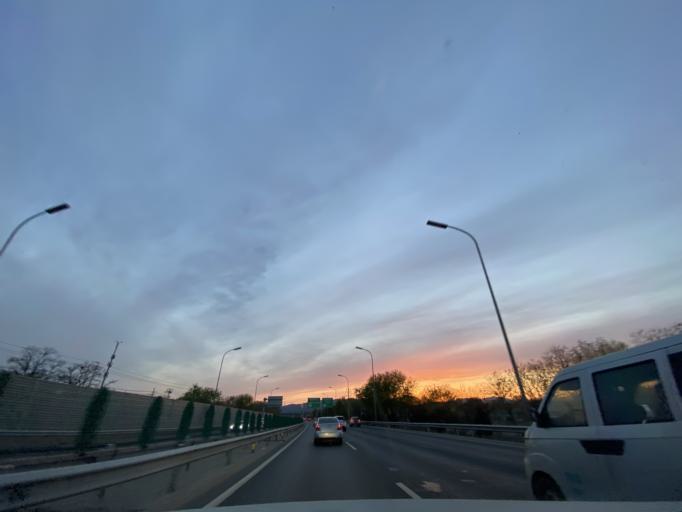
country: CN
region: Beijing
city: Haidian
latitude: 40.0159
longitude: 116.3030
